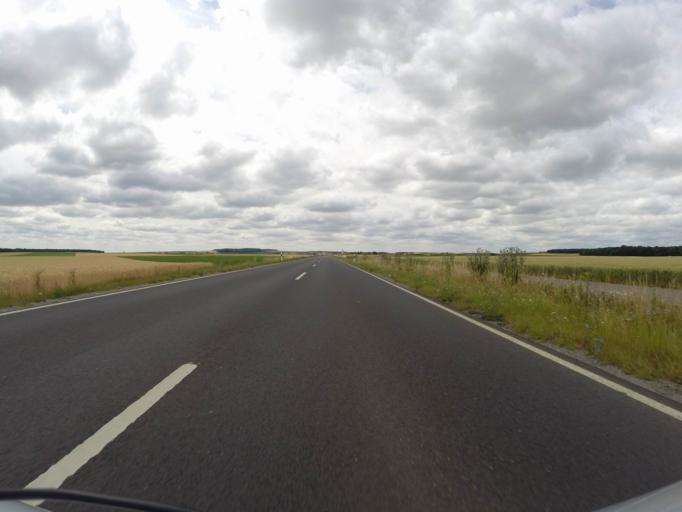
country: DE
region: Bavaria
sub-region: Regierungsbezirk Unterfranken
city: Kolitzheim
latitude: 49.9298
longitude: 10.2486
